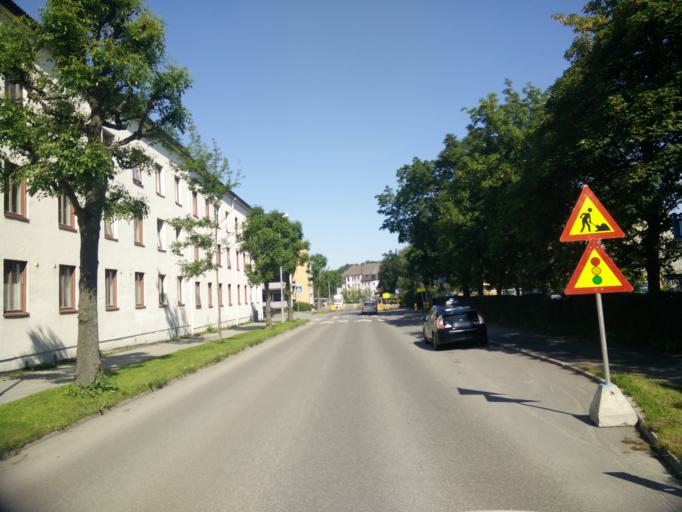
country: NO
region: Sor-Trondelag
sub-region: Trondheim
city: Trondheim
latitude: 63.4383
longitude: 10.4348
